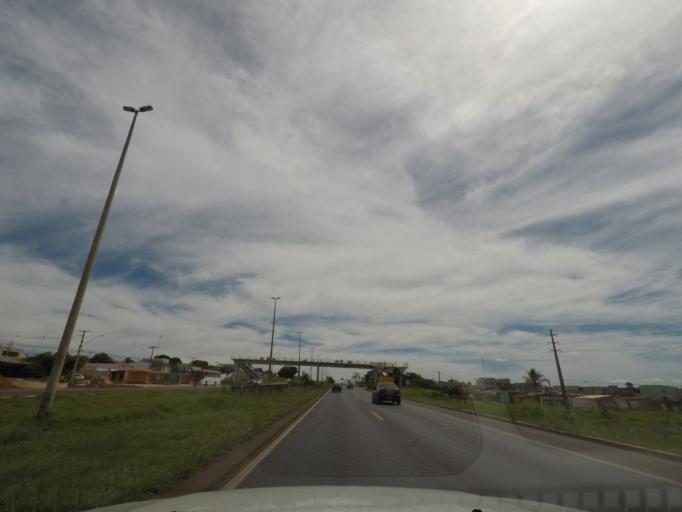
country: BR
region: Goias
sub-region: Planaltina
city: Planaltina
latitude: -15.6042
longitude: -47.6862
